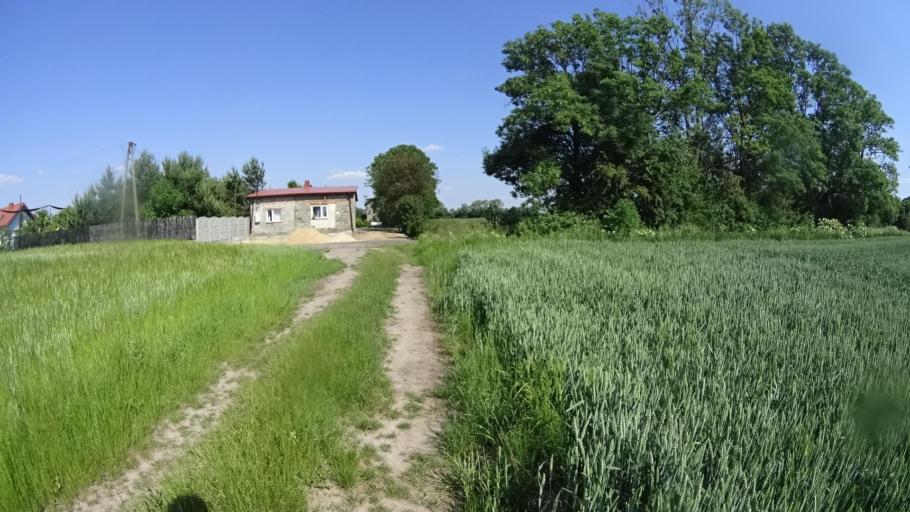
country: PL
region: Masovian Voivodeship
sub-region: Powiat grodziski
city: Milanowek
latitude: 52.1599
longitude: 20.6640
